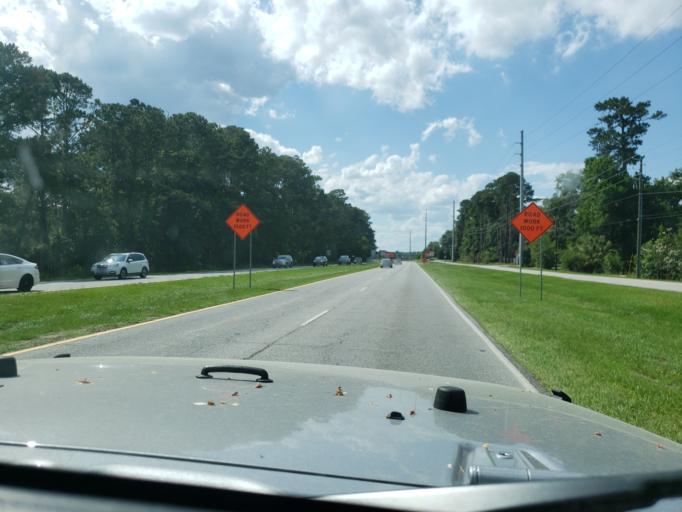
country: US
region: Georgia
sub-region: Chatham County
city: Whitemarsh Island
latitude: 32.0544
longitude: -81.0161
